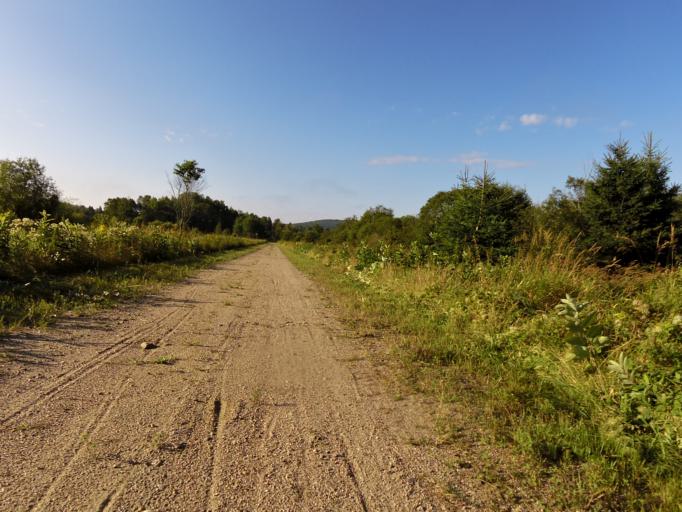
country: CA
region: Quebec
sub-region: Outaouais
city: Maniwaki
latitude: 46.2945
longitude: -76.0243
